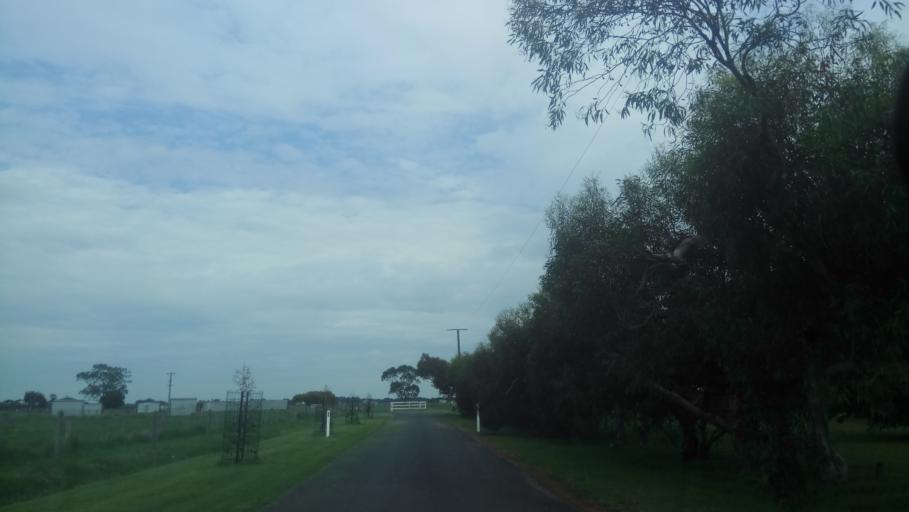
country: AU
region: Victoria
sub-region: Kingston
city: Chelsea Heights
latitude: -38.0306
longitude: 145.1419
